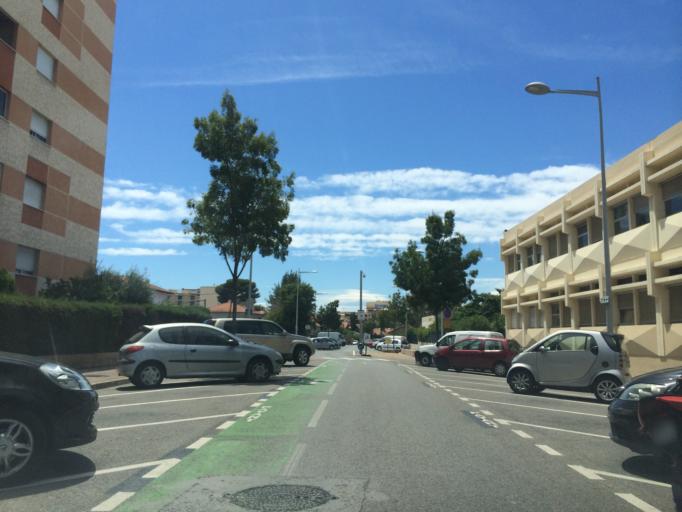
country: FR
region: Provence-Alpes-Cote d'Azur
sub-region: Departement des Alpes-Maritimes
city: Cagnes-sur-Mer
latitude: 43.6574
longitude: 7.1604
